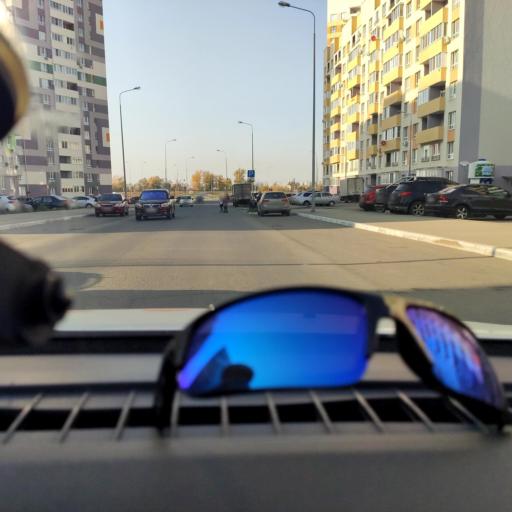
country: RU
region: Samara
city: Samara
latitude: 53.0939
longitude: 50.1615
